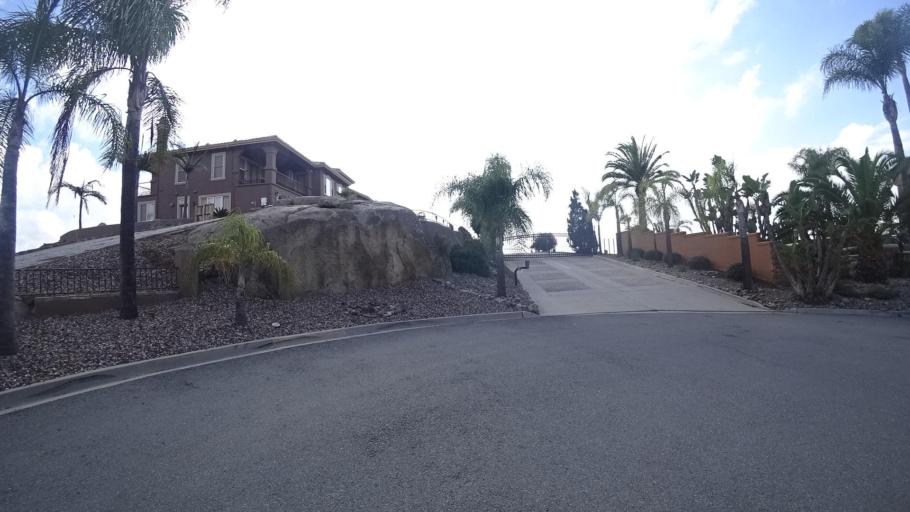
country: US
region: California
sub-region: San Diego County
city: Granite Hills
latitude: 32.7730
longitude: -116.8970
